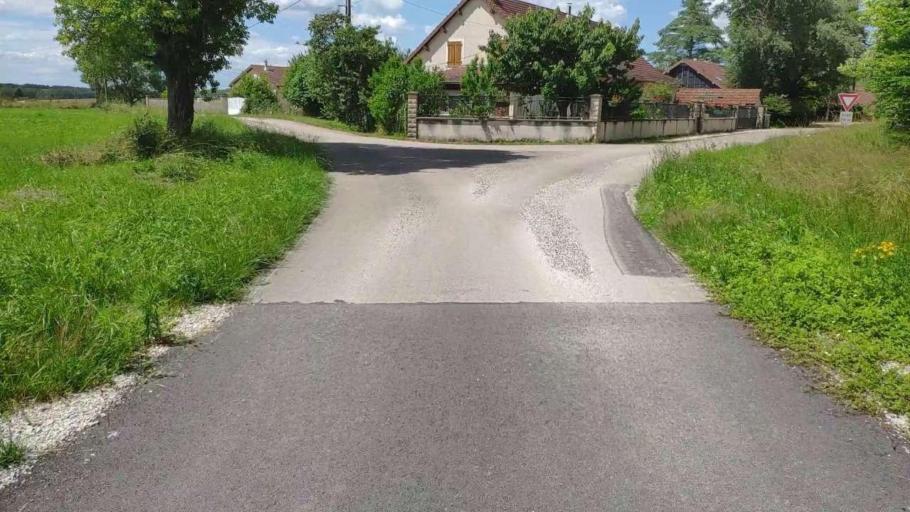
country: FR
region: Franche-Comte
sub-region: Departement du Jura
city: Chaussin
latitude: 46.8845
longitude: 5.4646
